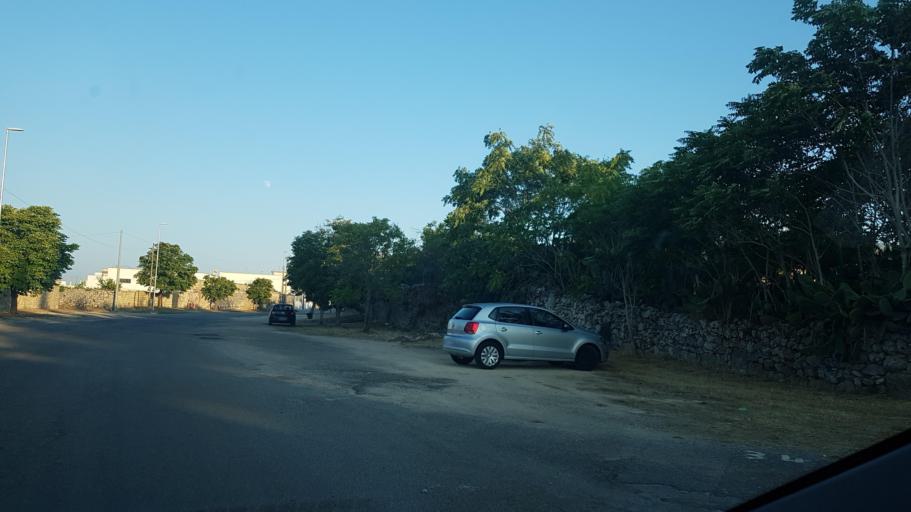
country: IT
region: Apulia
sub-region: Provincia di Lecce
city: Specchia
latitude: 39.9480
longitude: 18.2950
